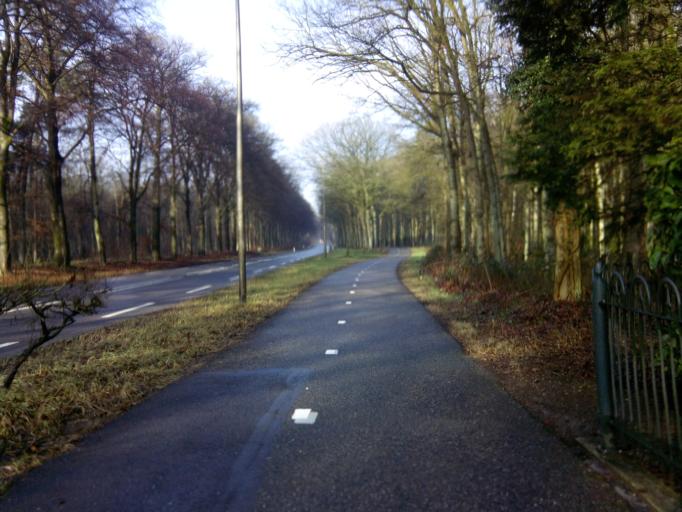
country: NL
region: Utrecht
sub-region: Gemeente Utrechtse Heuvelrug
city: Leersum
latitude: 52.0191
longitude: 5.4092
